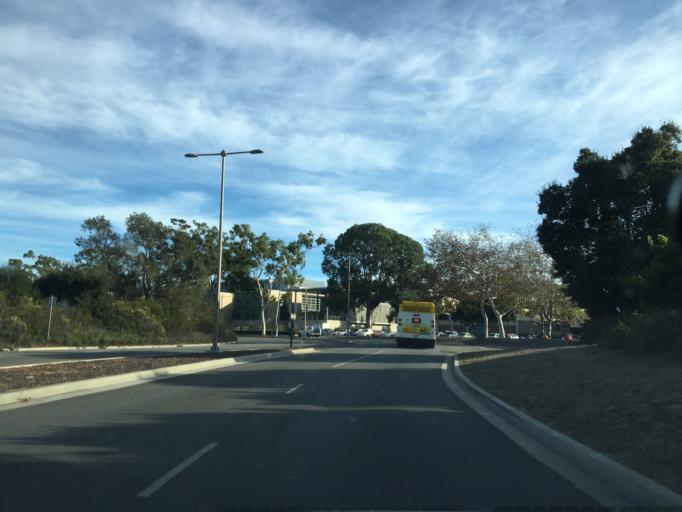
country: US
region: California
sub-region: Santa Barbara County
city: Isla Vista
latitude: 34.4167
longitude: -119.8429
